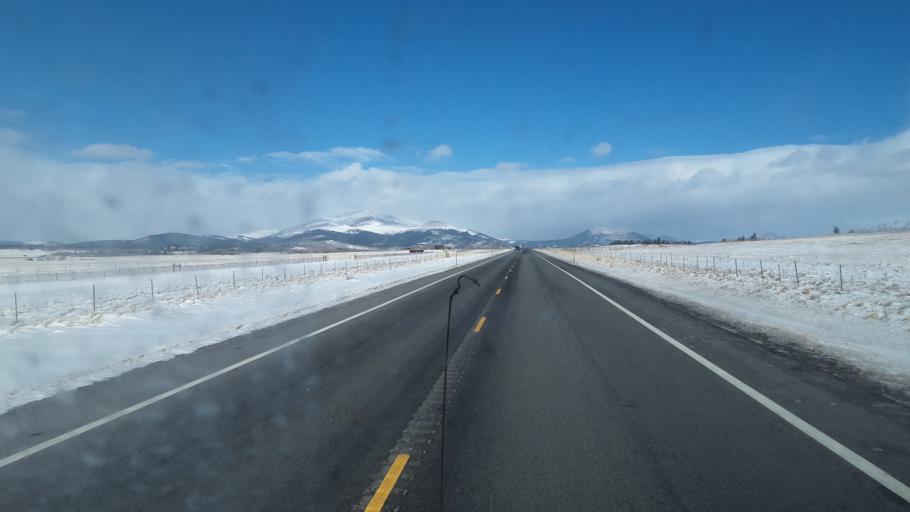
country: US
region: Colorado
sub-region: Park County
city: Fairplay
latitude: 39.1896
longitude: -105.9975
